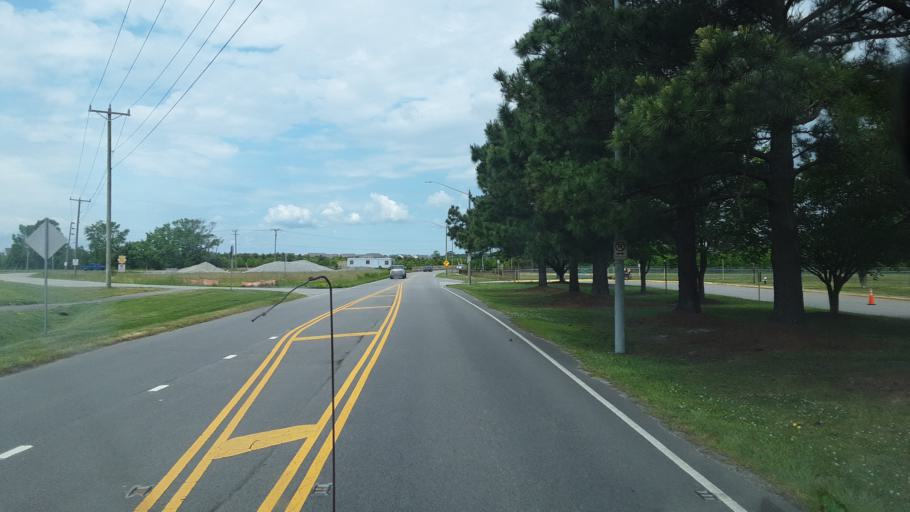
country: US
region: Virginia
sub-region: City of Virginia Beach
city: Virginia Beach
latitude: 36.7471
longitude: -76.0002
